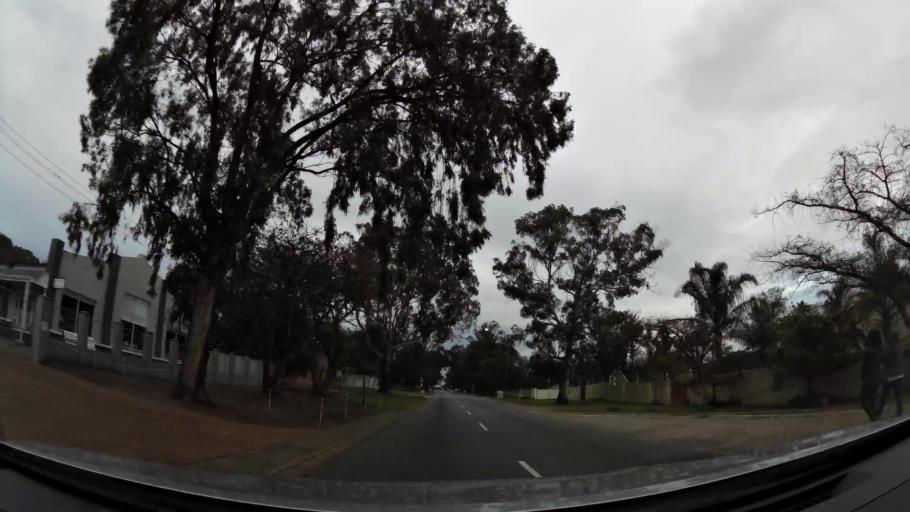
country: ZA
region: Eastern Cape
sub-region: Nelson Mandela Bay Metropolitan Municipality
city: Port Elizabeth
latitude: -33.9821
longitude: 25.5680
